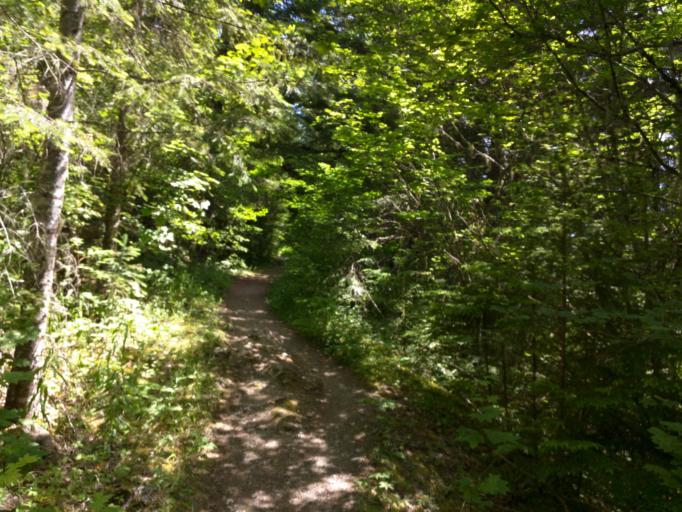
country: CA
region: British Columbia
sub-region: Fraser Valley Regional District
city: Chilliwack
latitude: 48.9136
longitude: -121.8535
